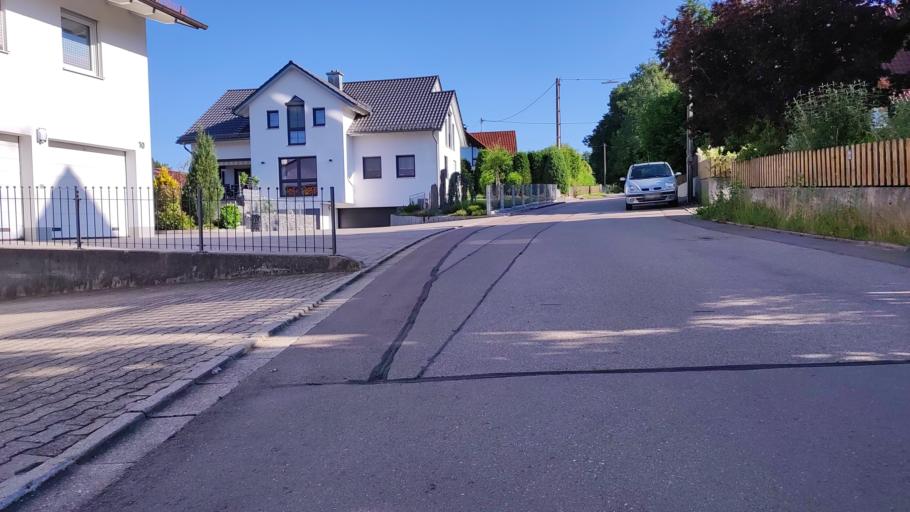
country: DE
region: Bavaria
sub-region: Swabia
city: Horgau
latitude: 48.3955
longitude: 10.6874
